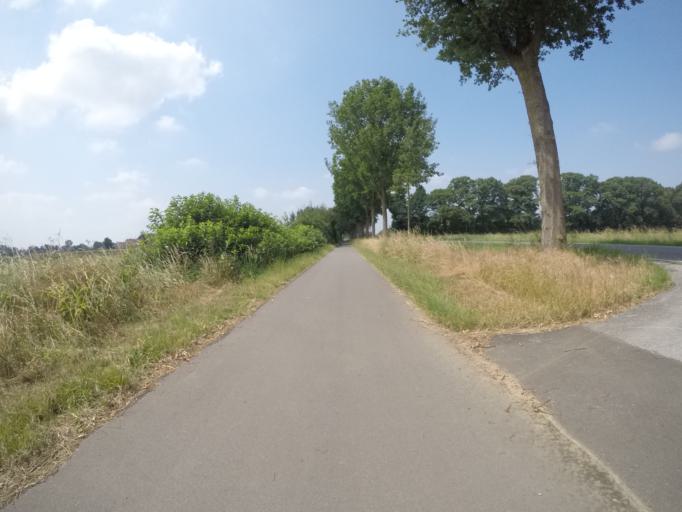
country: DE
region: North Rhine-Westphalia
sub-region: Regierungsbezirk Dusseldorf
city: Bocholt
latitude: 51.8436
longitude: 6.5430
